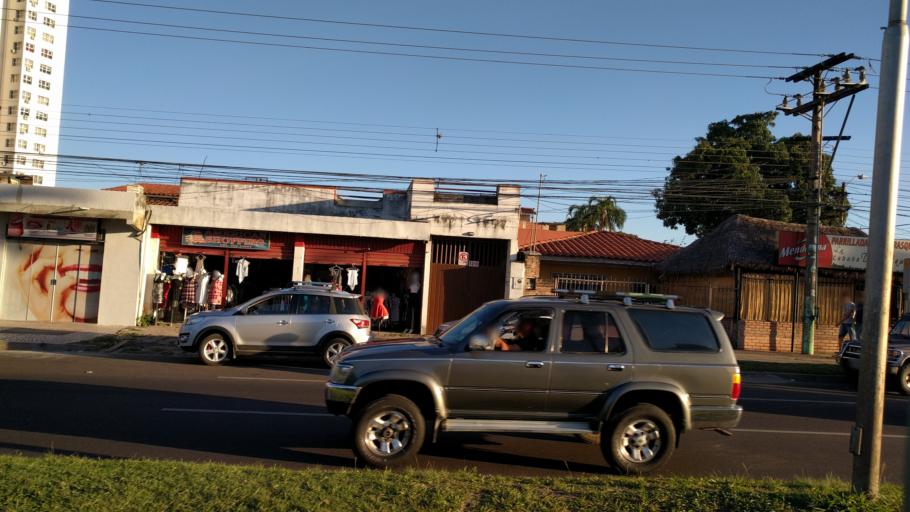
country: BO
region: Santa Cruz
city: Santa Cruz de la Sierra
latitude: -17.7597
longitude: -63.1810
